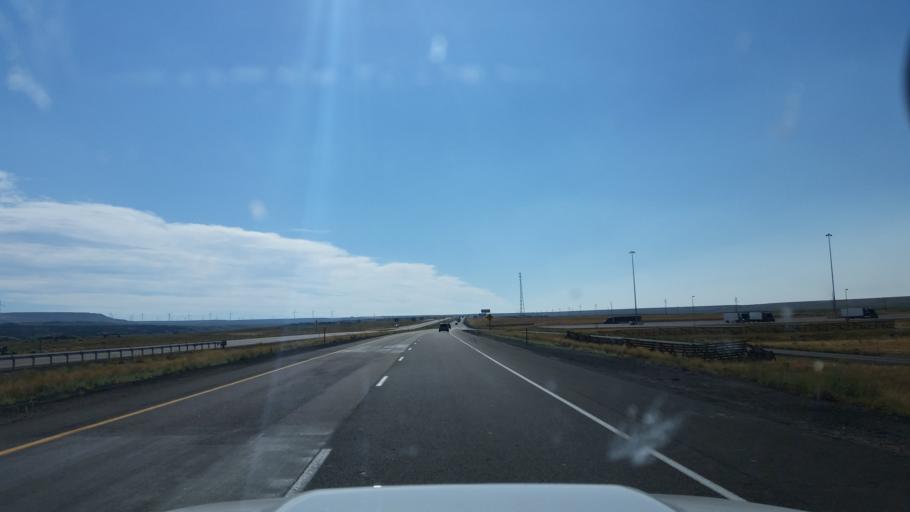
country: US
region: Wyoming
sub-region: Uinta County
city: Mountain View
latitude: 41.3316
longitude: -110.4297
